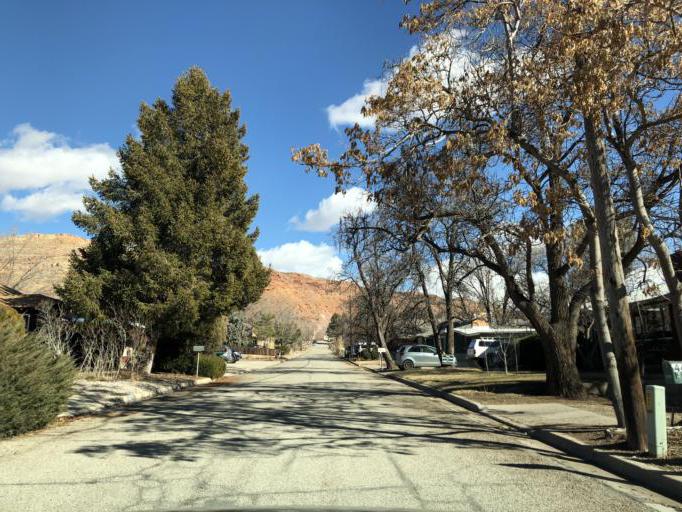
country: US
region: Utah
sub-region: Grand County
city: Moab
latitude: 38.5722
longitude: -109.5422
